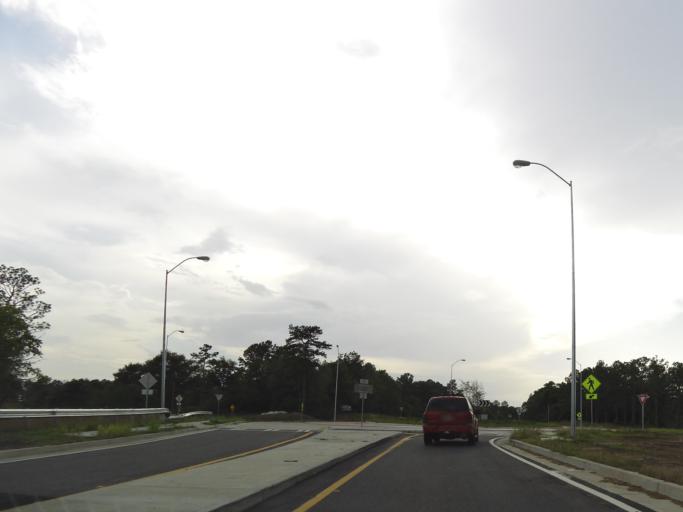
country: US
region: Georgia
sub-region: Bibb County
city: West Point
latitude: 32.8006
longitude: -83.8017
